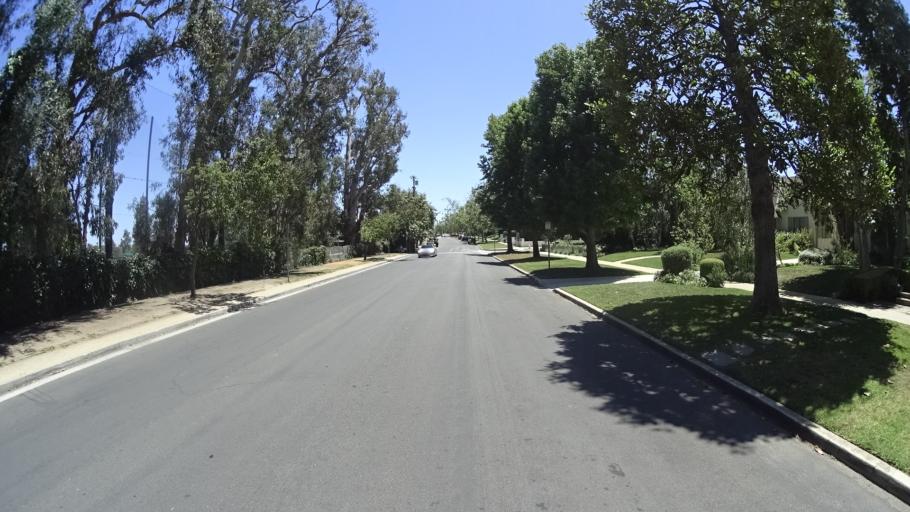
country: US
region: California
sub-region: Los Angeles County
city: Santa Monica
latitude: 34.0484
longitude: -118.4860
